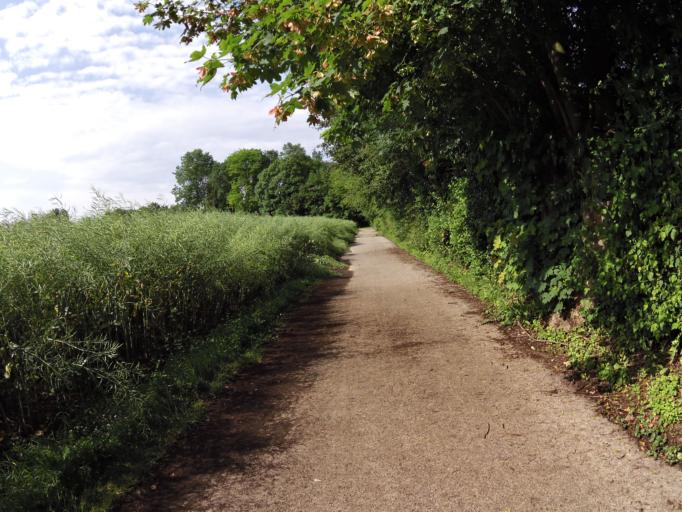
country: FR
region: Champagne-Ardenne
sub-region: Departement de l'Aube
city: Saint-Julien-les-Villas
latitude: 48.2678
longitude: 4.1105
